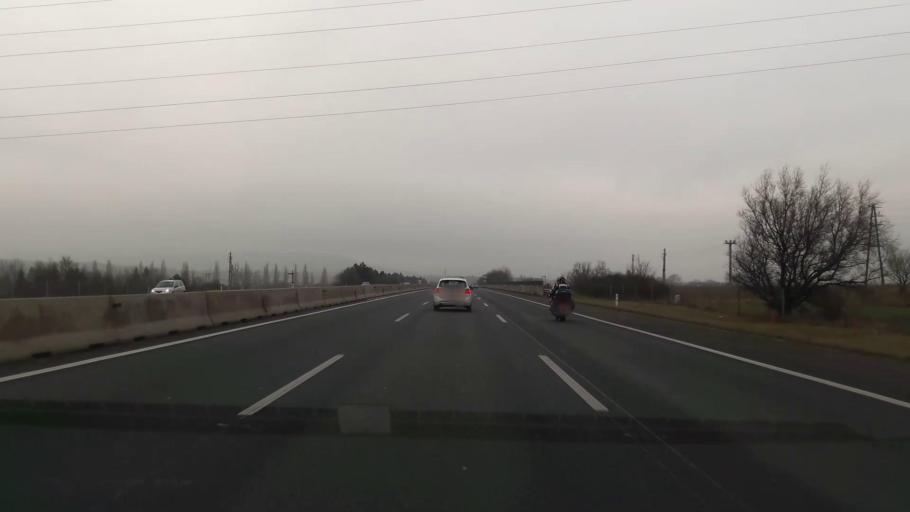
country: AT
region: Lower Austria
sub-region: Politischer Bezirk Baden
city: Leobersdorf
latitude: 47.9160
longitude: 16.2086
